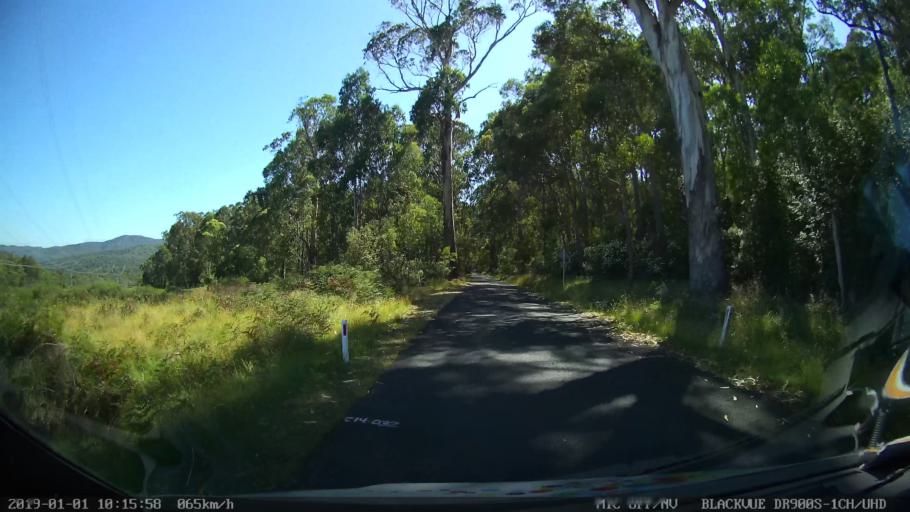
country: AU
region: New South Wales
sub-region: Snowy River
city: Jindabyne
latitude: -36.0967
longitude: 148.1632
